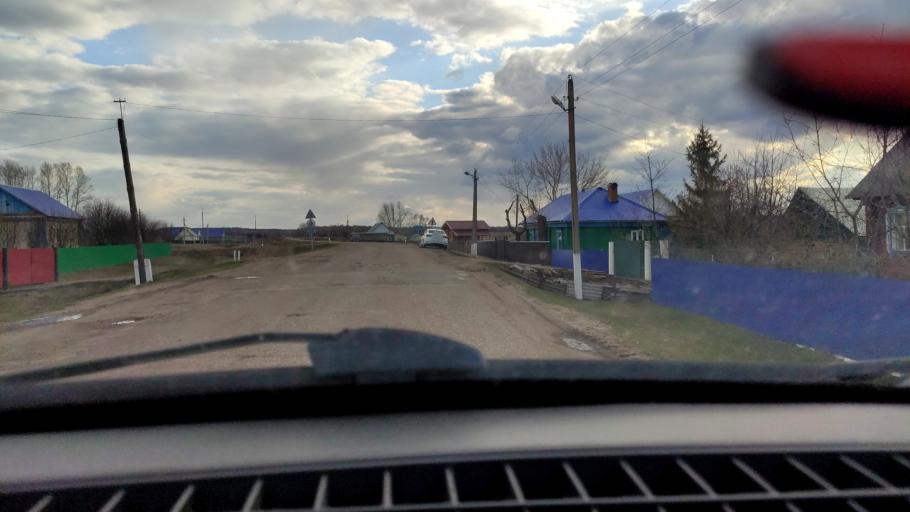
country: RU
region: Bashkortostan
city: Karmaskaly
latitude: 54.3333
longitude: 55.9950
